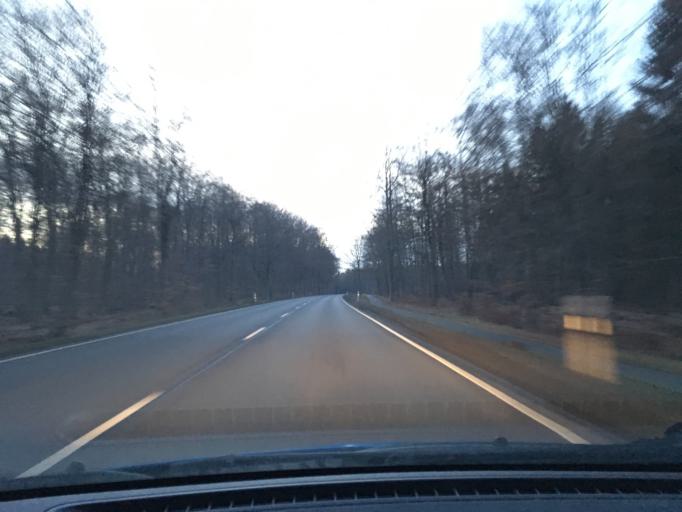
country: DE
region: Lower Saxony
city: Reinstorf
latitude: 53.2233
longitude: 10.5578
